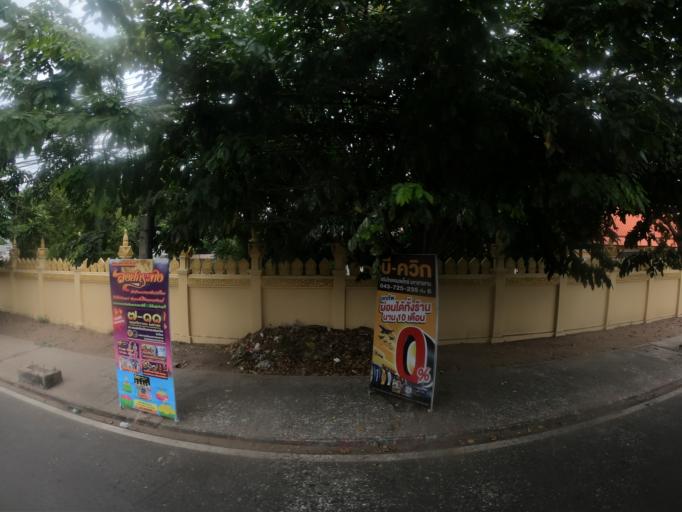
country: TH
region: Maha Sarakham
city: Maha Sarakham
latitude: 16.1798
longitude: 103.3062
